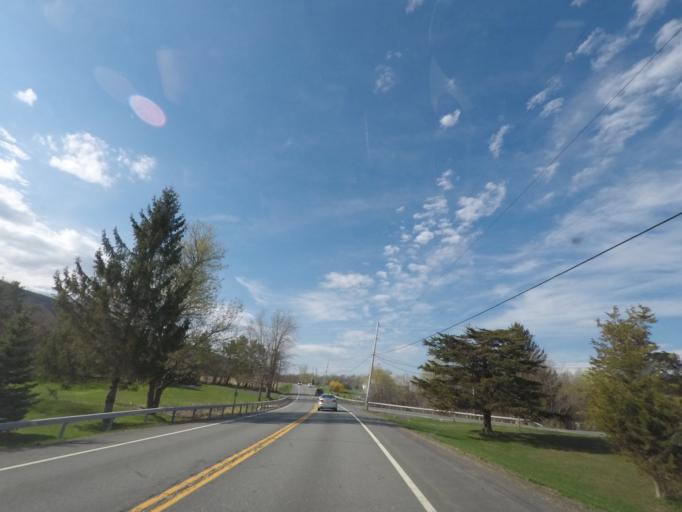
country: US
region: New York
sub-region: Albany County
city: Voorheesville
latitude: 42.6104
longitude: -73.9715
